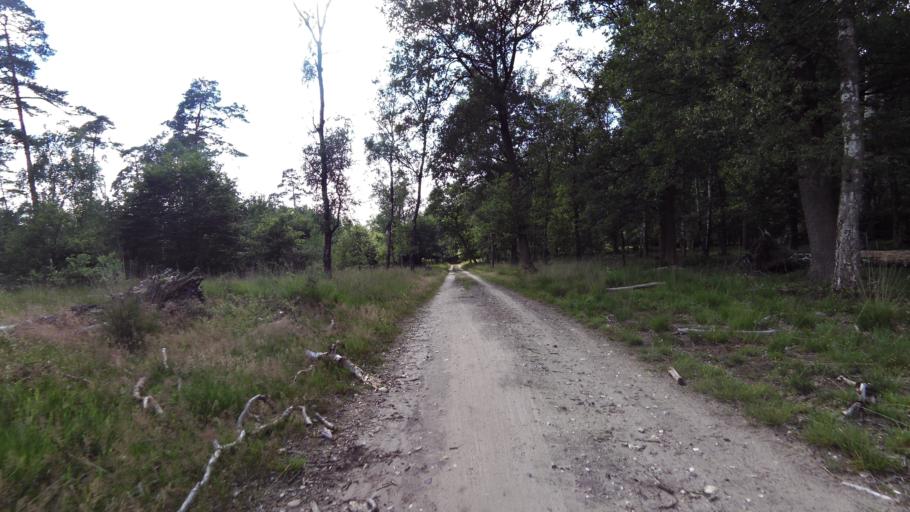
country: NL
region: Gelderland
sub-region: Gemeente Apeldoorn
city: Uddel
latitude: 52.2920
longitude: 5.8702
